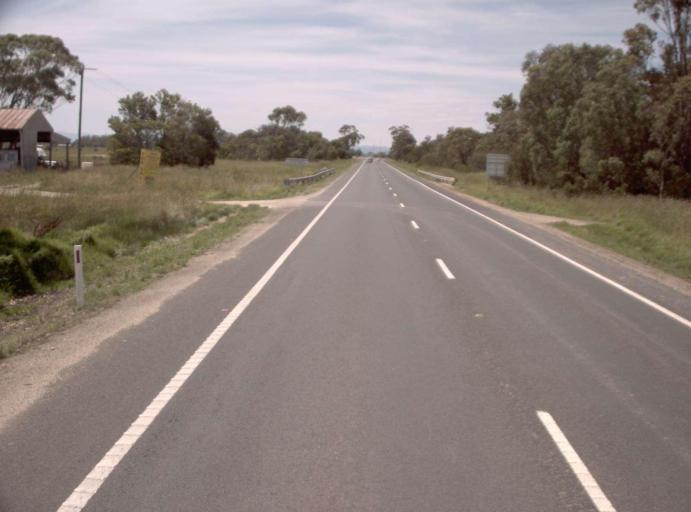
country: AU
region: Victoria
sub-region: Wellington
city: Sale
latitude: -38.0736
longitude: 147.0729
